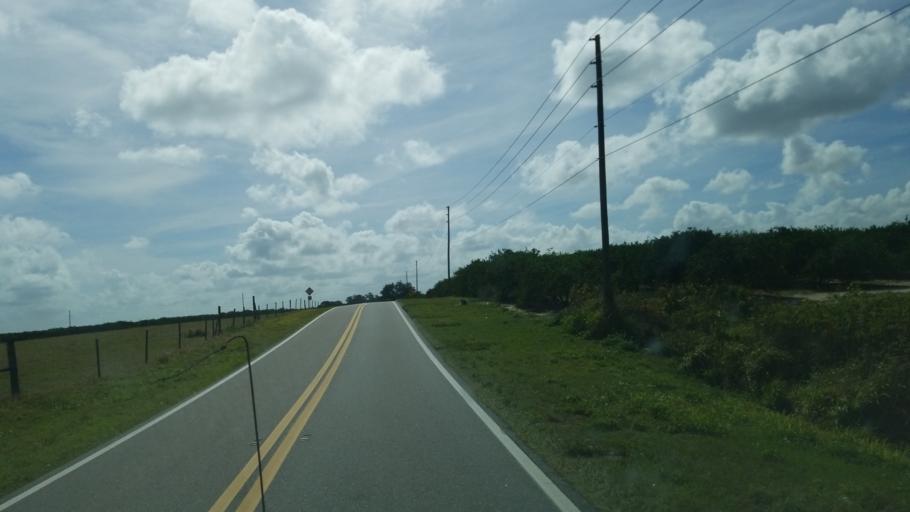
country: US
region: Florida
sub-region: Polk County
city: Lake Wales
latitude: 27.9243
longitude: -81.4965
